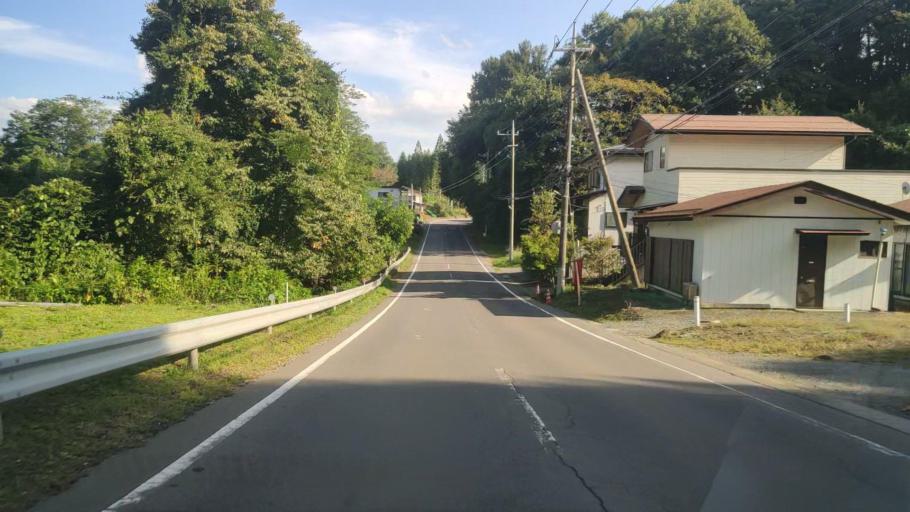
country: JP
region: Nagano
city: Komoro
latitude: 36.5443
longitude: 138.5557
